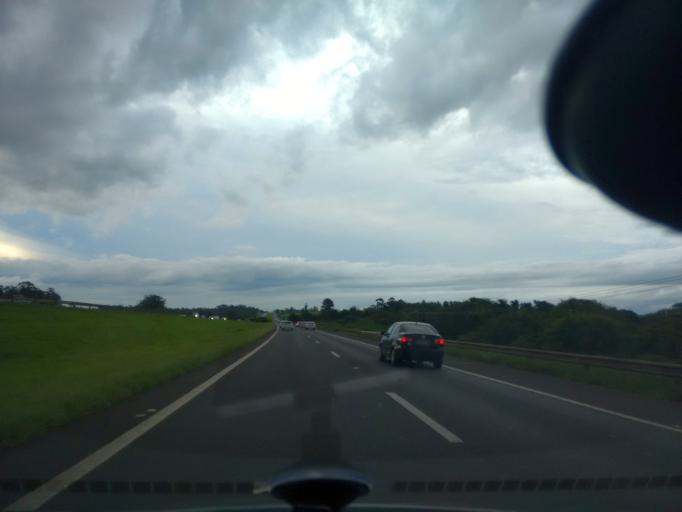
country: BR
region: Sao Paulo
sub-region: Rio Claro
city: Rio Claro
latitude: -22.3933
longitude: -47.5993
